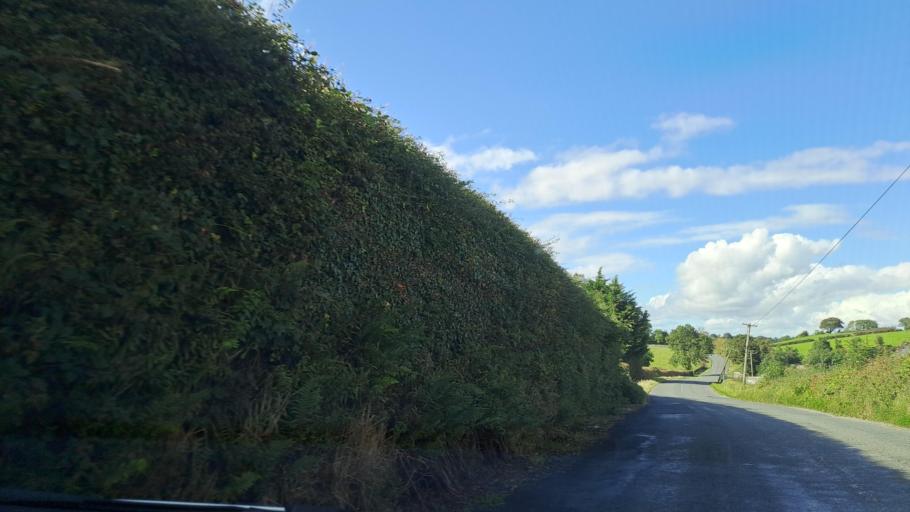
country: IE
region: Ulster
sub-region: An Cabhan
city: Kingscourt
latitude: 53.9582
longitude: -6.8460
